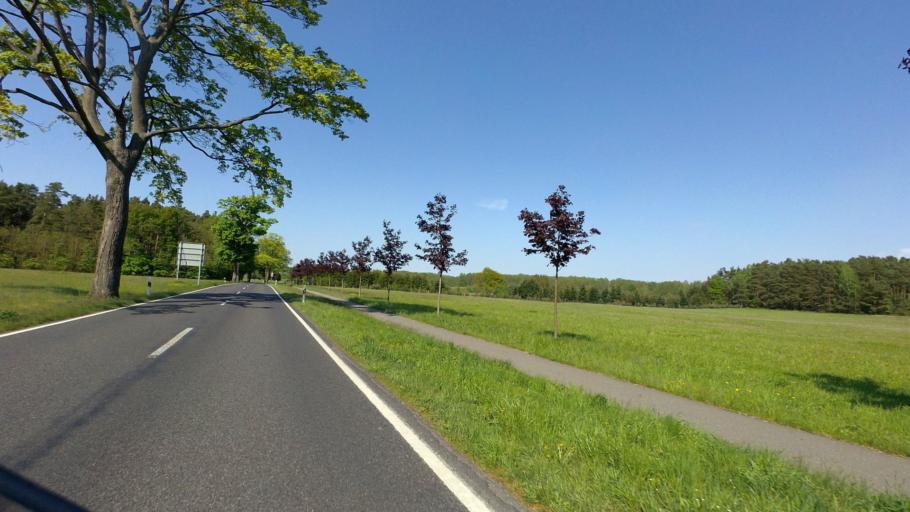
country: DE
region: Brandenburg
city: Neu Zauche
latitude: 52.0288
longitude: 14.0406
